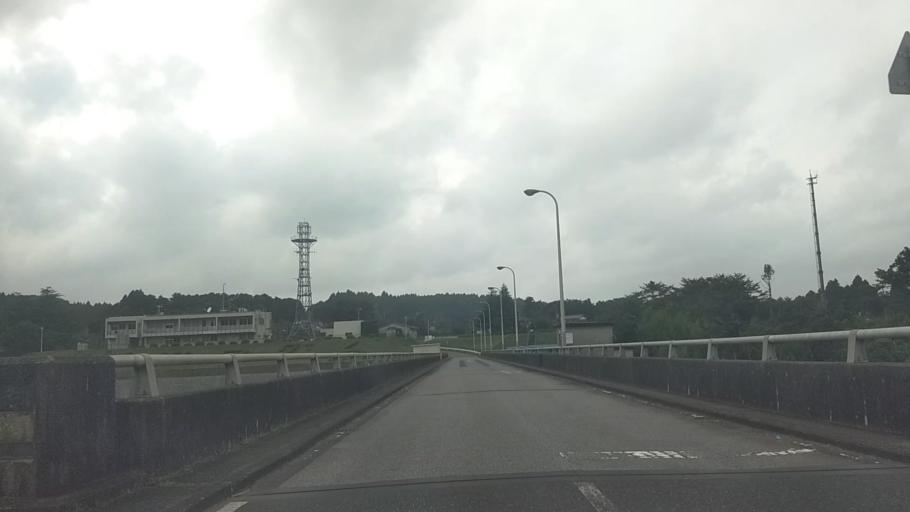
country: JP
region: Chiba
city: Kawaguchi
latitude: 35.2296
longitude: 140.0865
